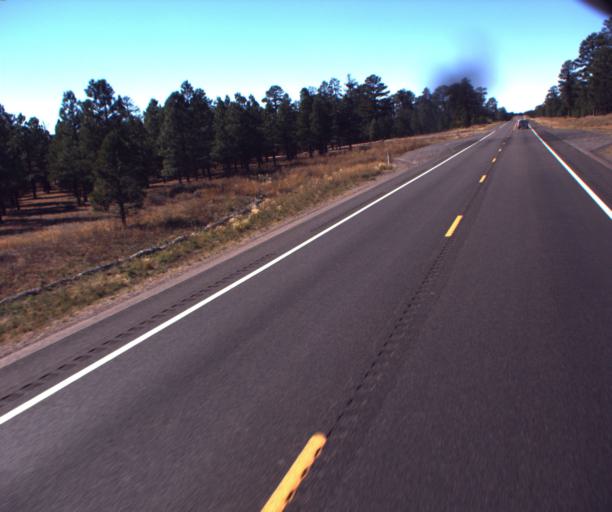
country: US
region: Arizona
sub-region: Apache County
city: Saint Michaels
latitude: 35.6994
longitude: -109.2866
